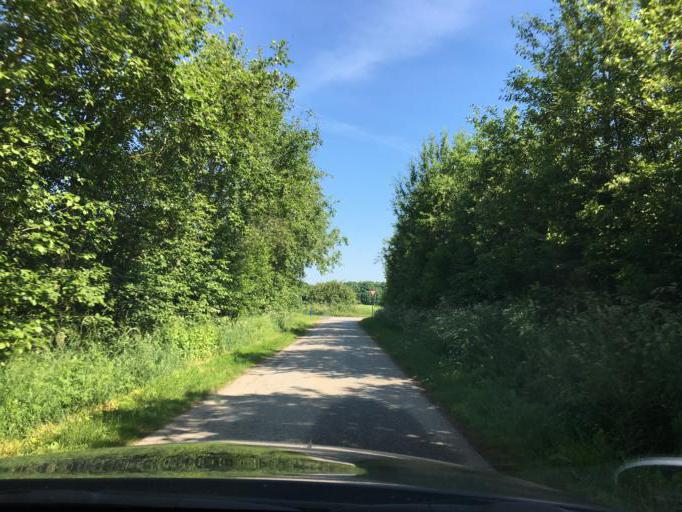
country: DK
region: South Denmark
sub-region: Kolding Kommune
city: Kolding
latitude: 55.5640
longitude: 9.4767
